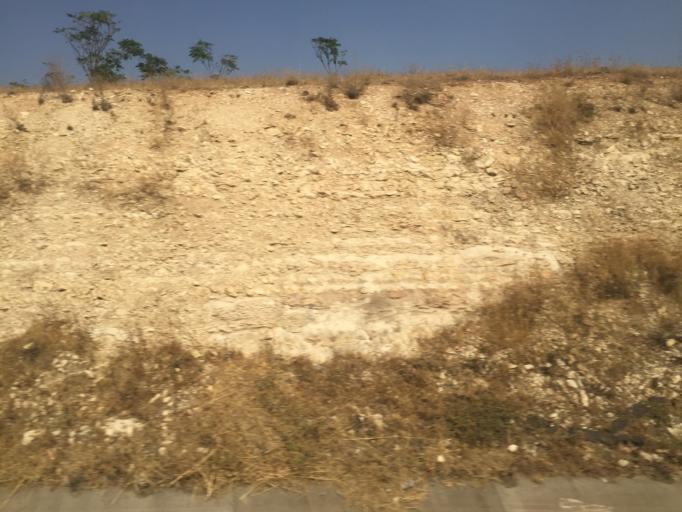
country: TR
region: Sanliurfa
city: Akziyaret
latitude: 37.2685
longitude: 38.8015
